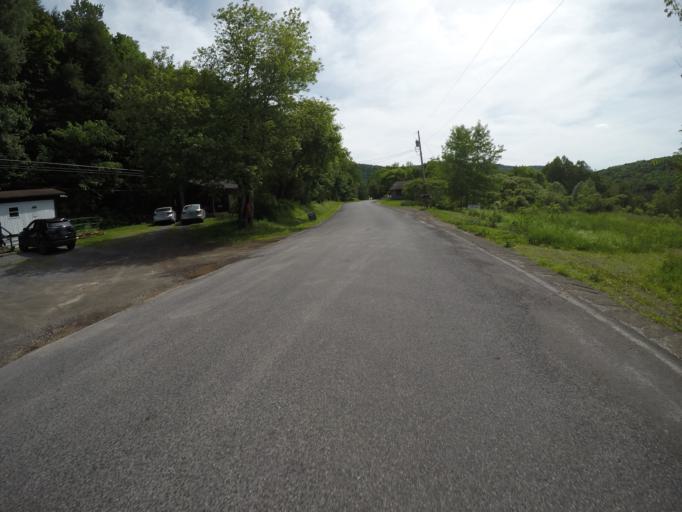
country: US
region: New York
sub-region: Sullivan County
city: Livingston Manor
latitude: 42.1266
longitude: -74.6681
